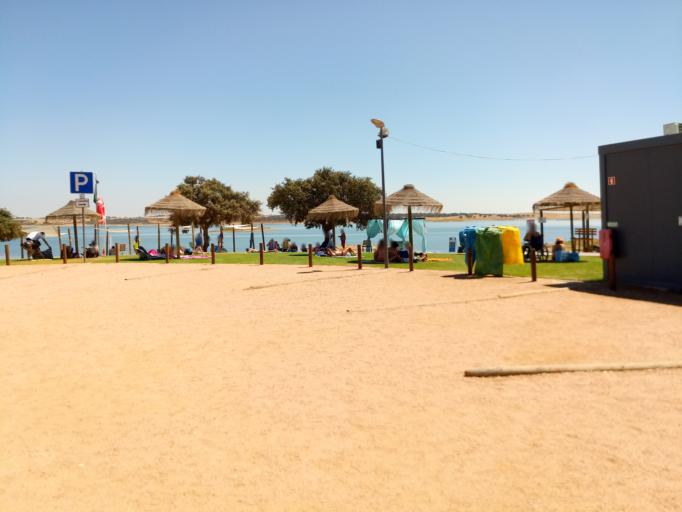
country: PT
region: Evora
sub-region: Mourao
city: Mourao
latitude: 38.4346
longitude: -7.3506
